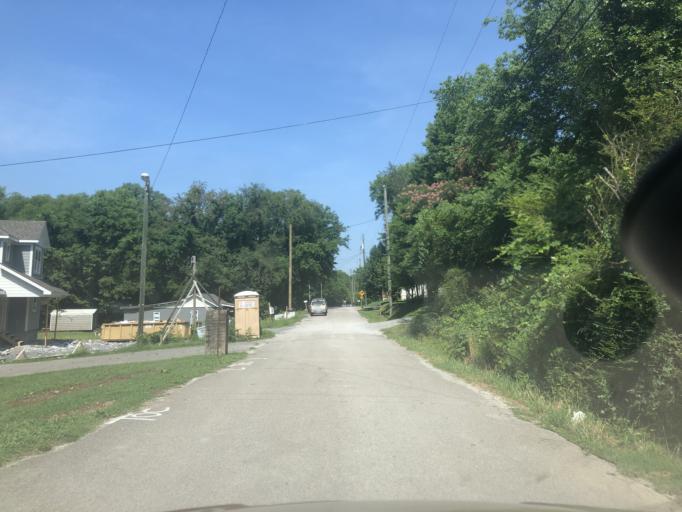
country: US
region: Tennessee
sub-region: Davidson County
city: Lakewood
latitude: 36.2240
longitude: -86.6271
